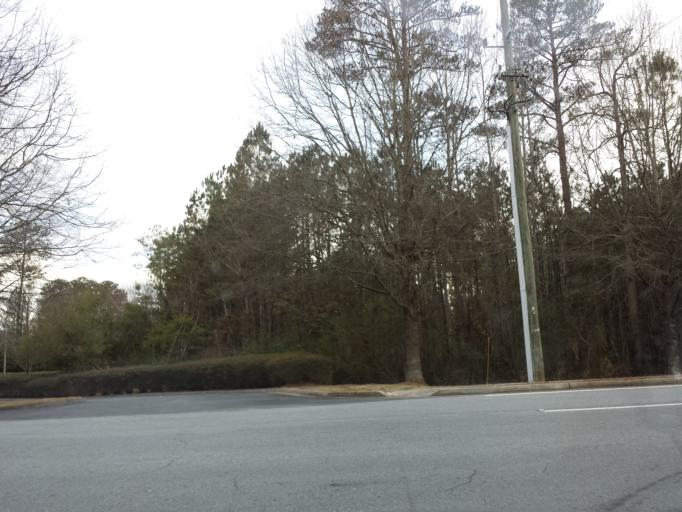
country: US
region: Georgia
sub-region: Cobb County
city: Smyrna
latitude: 33.9459
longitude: -84.4778
